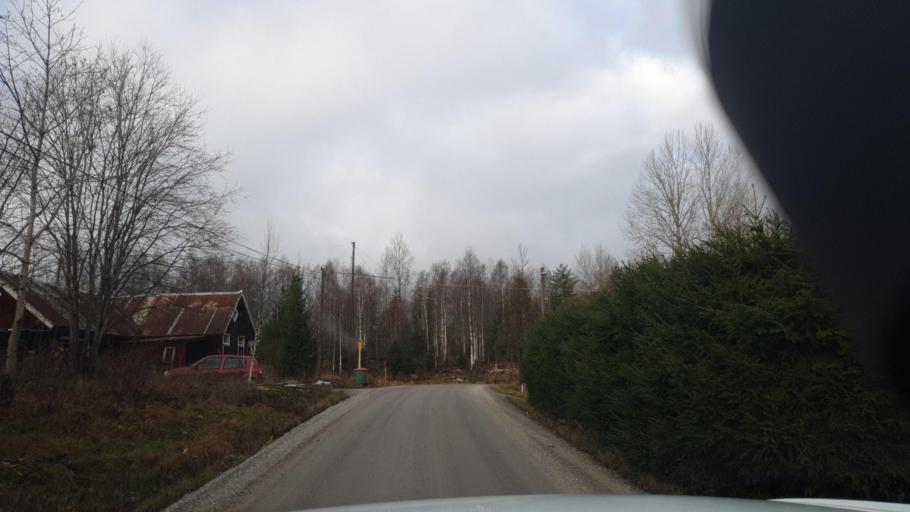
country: SE
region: Vaermland
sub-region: Sunne Kommun
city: Sunne
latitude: 59.6987
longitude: 12.8844
